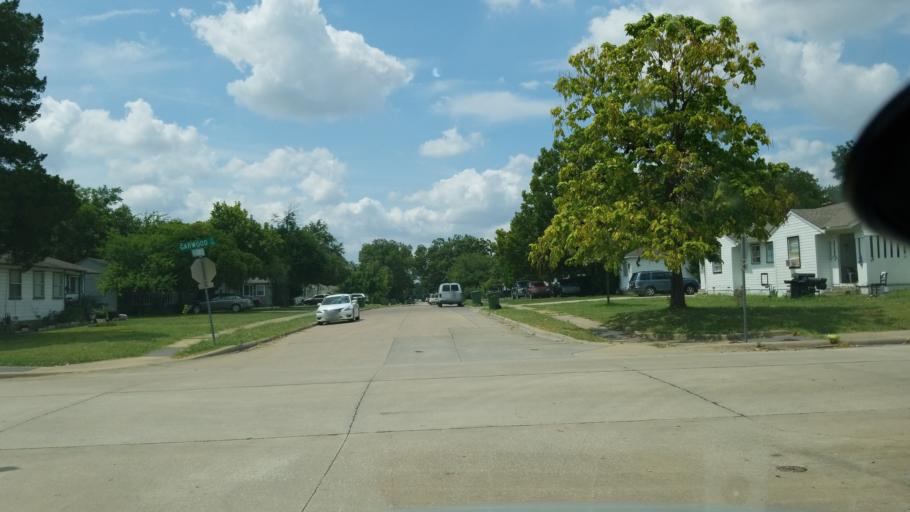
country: US
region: Texas
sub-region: Dallas County
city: Garland
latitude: 32.9199
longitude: -96.6518
